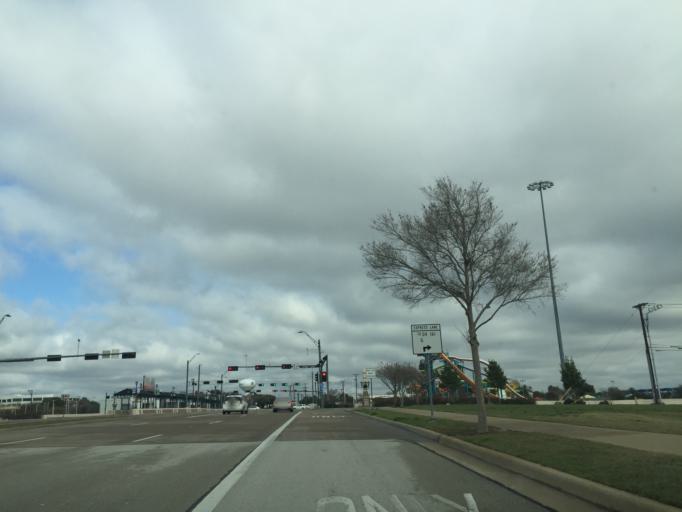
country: US
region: Texas
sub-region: Tarrant County
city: Arlington
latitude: 32.7583
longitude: -97.0851
